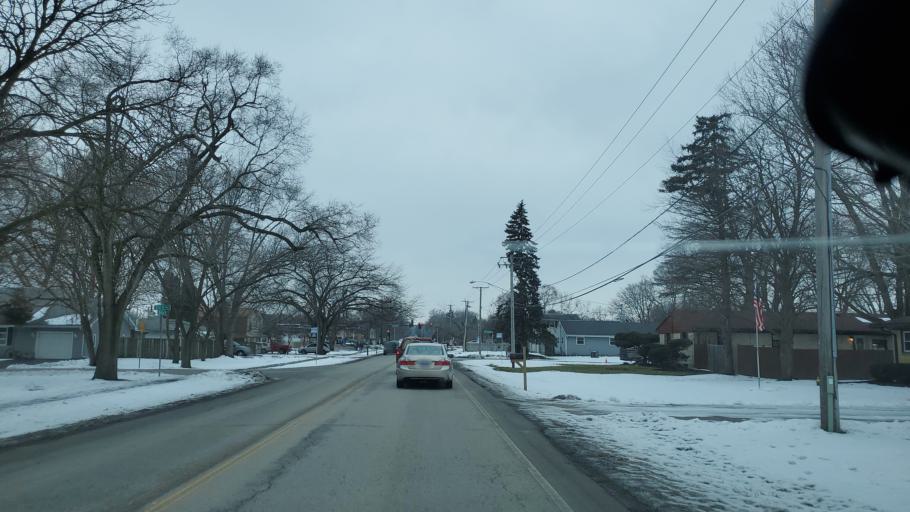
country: US
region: Illinois
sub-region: Kane County
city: North Aurora
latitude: 41.7939
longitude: -88.2794
